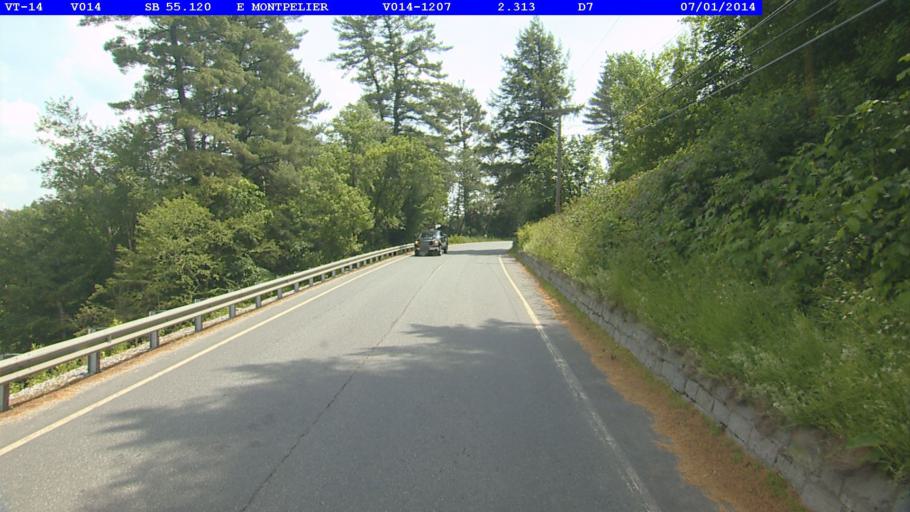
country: US
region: Vermont
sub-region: Washington County
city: Barre
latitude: 44.2665
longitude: -72.4872
